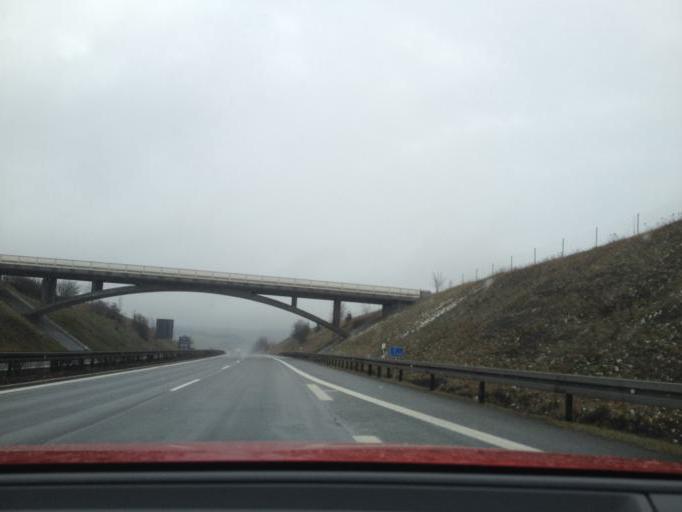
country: DE
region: Bavaria
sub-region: Upper Franconia
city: Regnitzlosau
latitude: 50.3066
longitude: 12.0241
